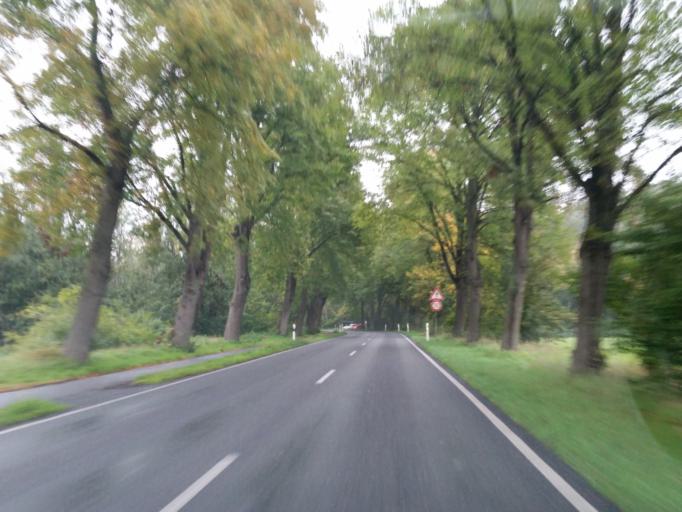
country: DE
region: Lower Saxony
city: Cremlingen
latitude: 52.2574
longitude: 10.5924
